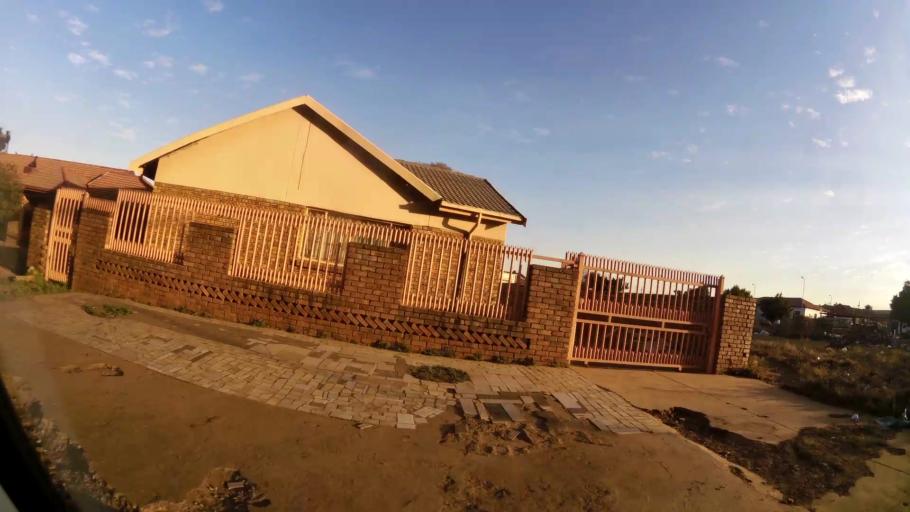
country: ZA
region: Gauteng
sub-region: City of Tshwane Metropolitan Municipality
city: Cullinan
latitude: -25.7084
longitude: 28.3666
